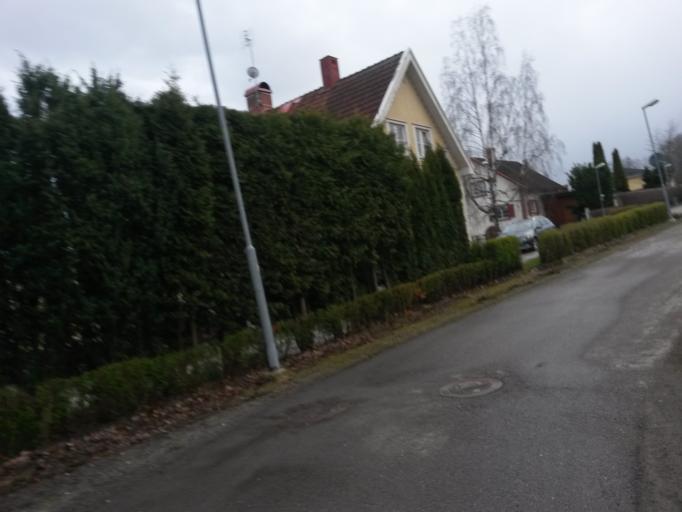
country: SE
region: OErebro
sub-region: Karlskoga Kommun
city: Karlskoga
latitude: 59.3243
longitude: 14.5266
